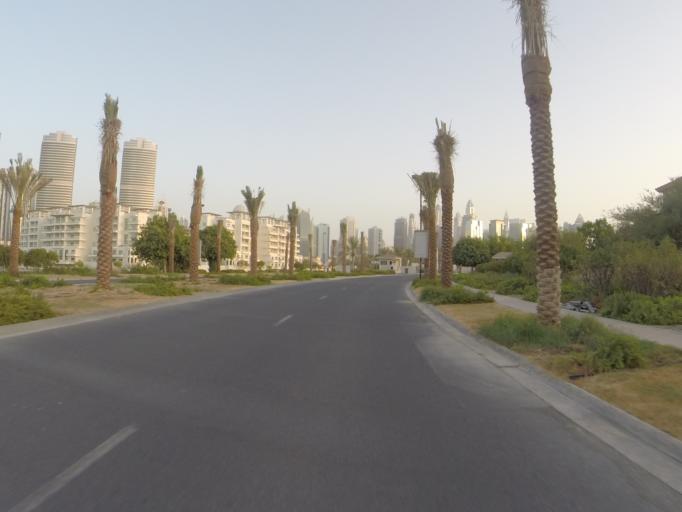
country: AE
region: Dubai
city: Dubai
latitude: 25.0648
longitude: 55.1508
